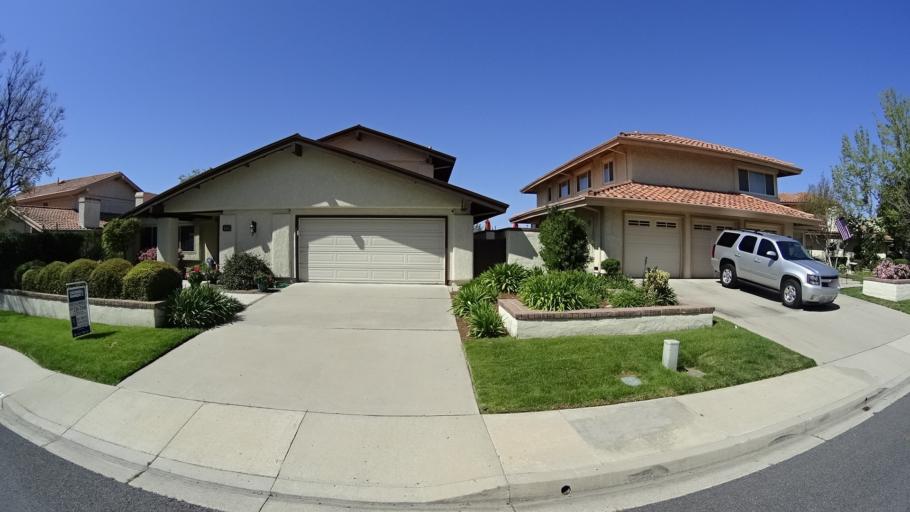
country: US
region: California
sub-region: Ventura County
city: Moorpark
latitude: 34.2344
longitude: -118.8488
